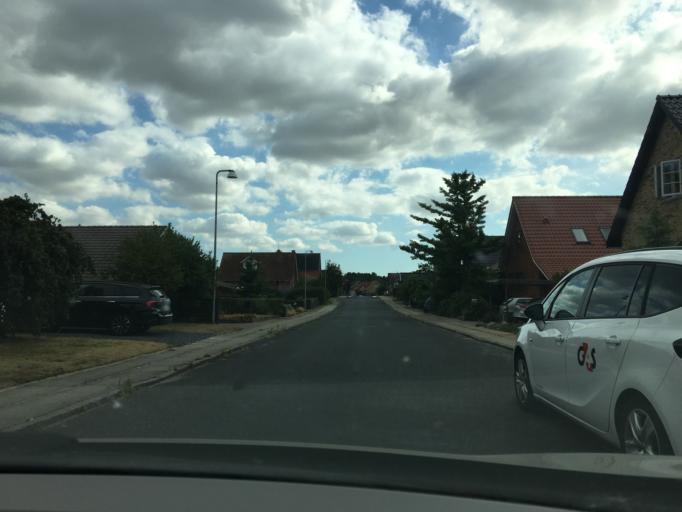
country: DK
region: South Denmark
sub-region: Odense Kommune
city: Odense
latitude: 55.3971
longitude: 10.3302
